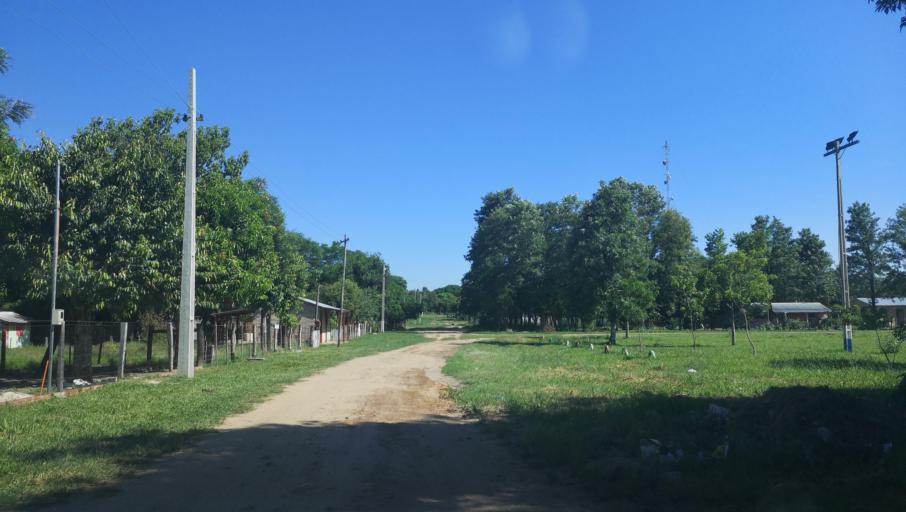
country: PY
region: Caaguazu
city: Carayao
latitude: -25.2051
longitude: -56.3958
